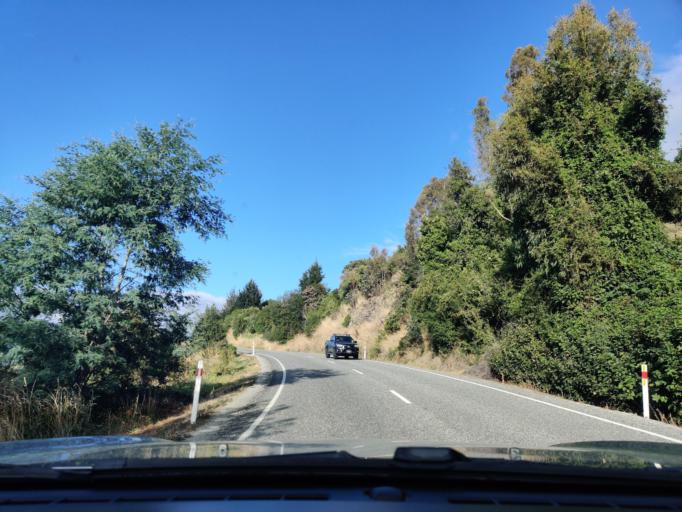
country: NZ
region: Otago
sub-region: Queenstown-Lakes District
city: Queenstown
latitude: -45.0409
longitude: 168.6372
